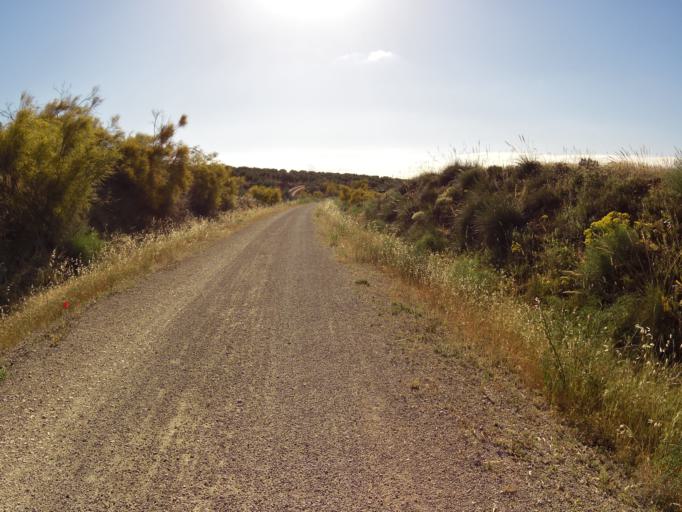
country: ES
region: Andalusia
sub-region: Province of Cordoba
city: Luque
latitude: 37.5835
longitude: -4.2009
